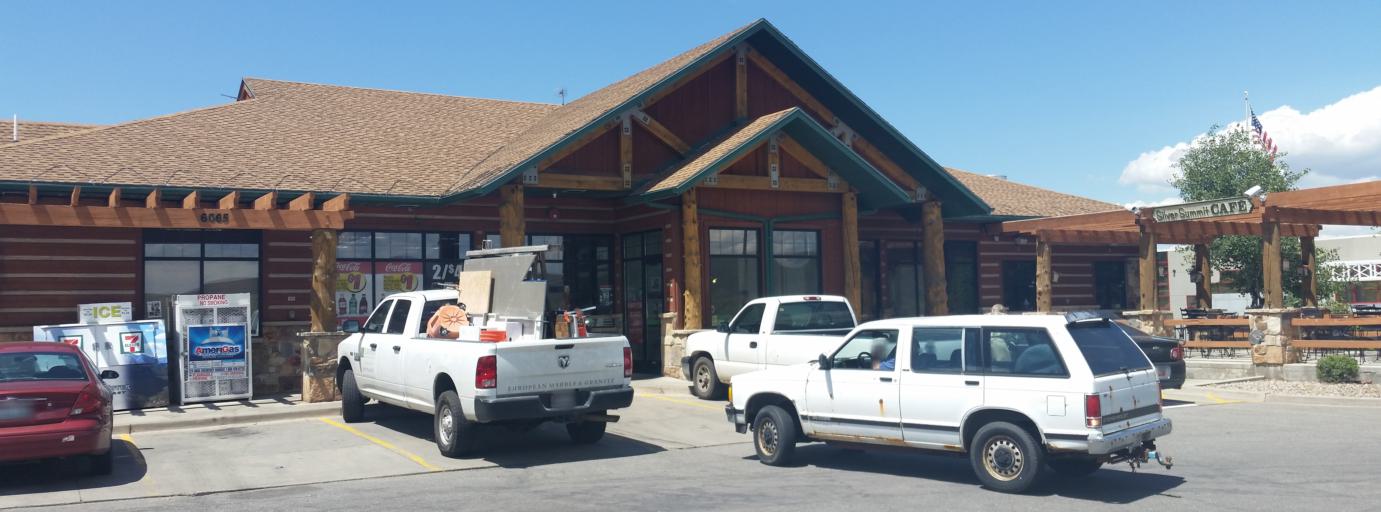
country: US
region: Utah
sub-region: Summit County
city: Snyderville
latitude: 40.7204
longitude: -111.4852
